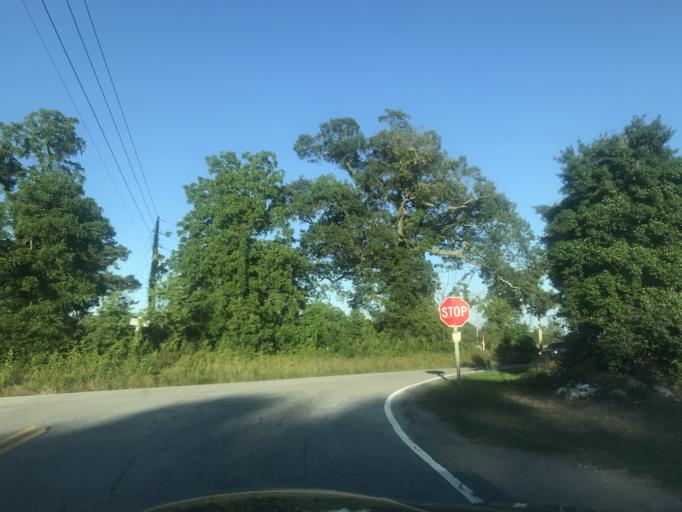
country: US
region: North Carolina
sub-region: Johnston County
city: Archer Lodge
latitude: 35.6931
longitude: -78.3738
